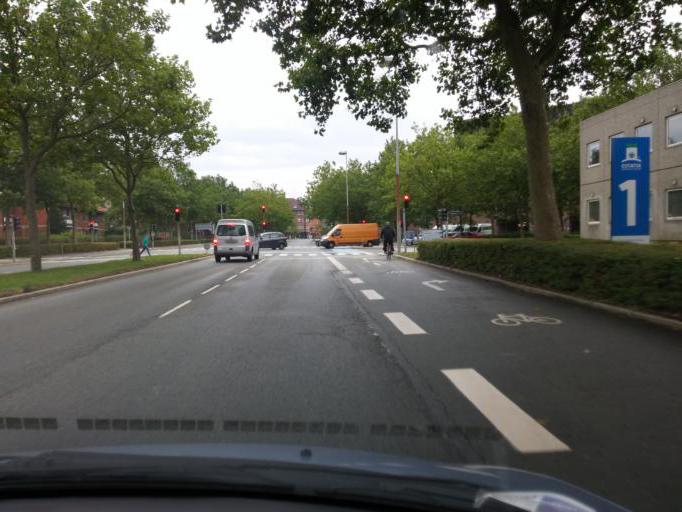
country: DK
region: South Denmark
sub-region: Odense Kommune
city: Odense
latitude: 55.4040
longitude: 10.3878
